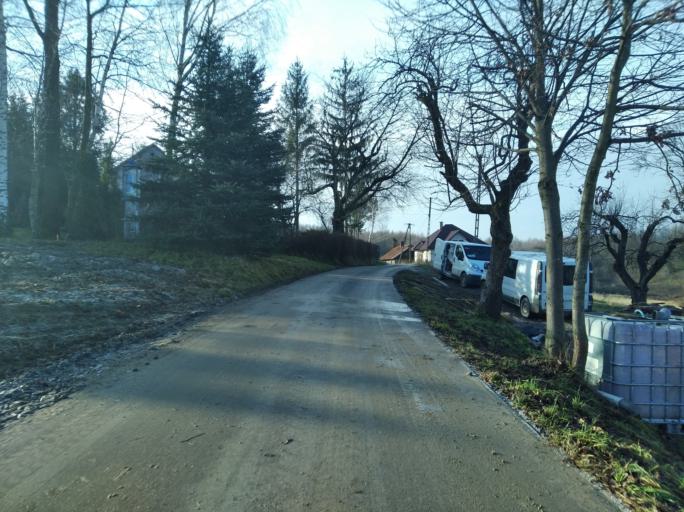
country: PL
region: Subcarpathian Voivodeship
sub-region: Powiat strzyzowski
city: Wysoka Strzyzowska
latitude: 49.8573
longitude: 21.7524
